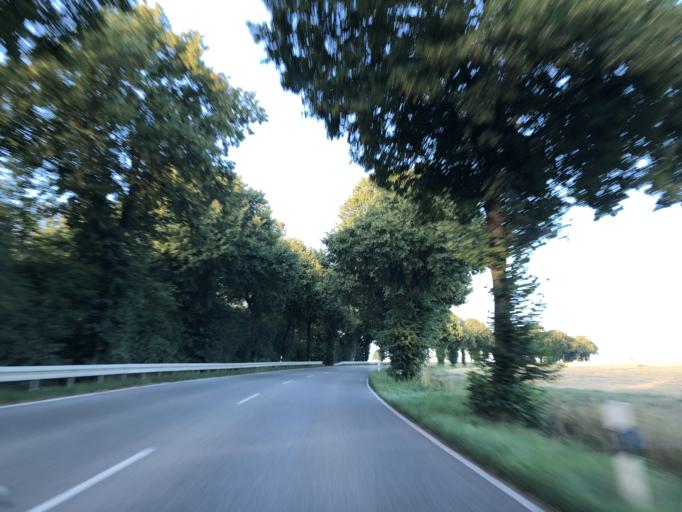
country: DE
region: Bavaria
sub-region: Upper Bavaria
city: Moosinning
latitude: 48.2573
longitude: 11.8539
